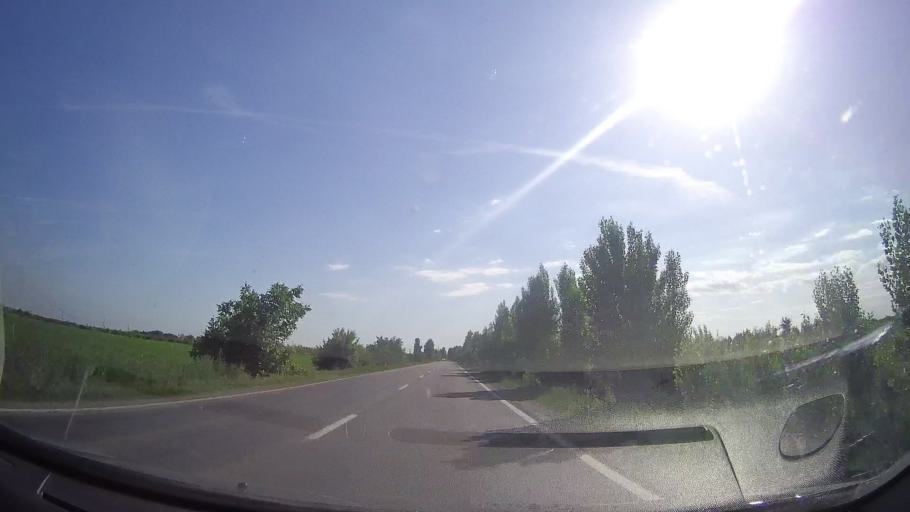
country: RO
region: Prahova
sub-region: Comuna Barcanesti
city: Barcanesti
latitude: 44.8955
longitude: 26.0549
